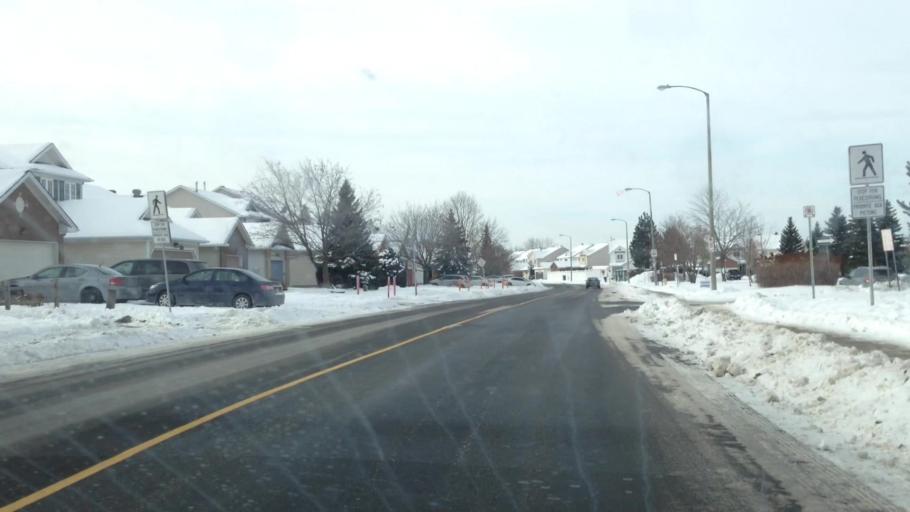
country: CA
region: Ontario
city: Clarence-Rockland
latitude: 45.4691
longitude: -75.4729
